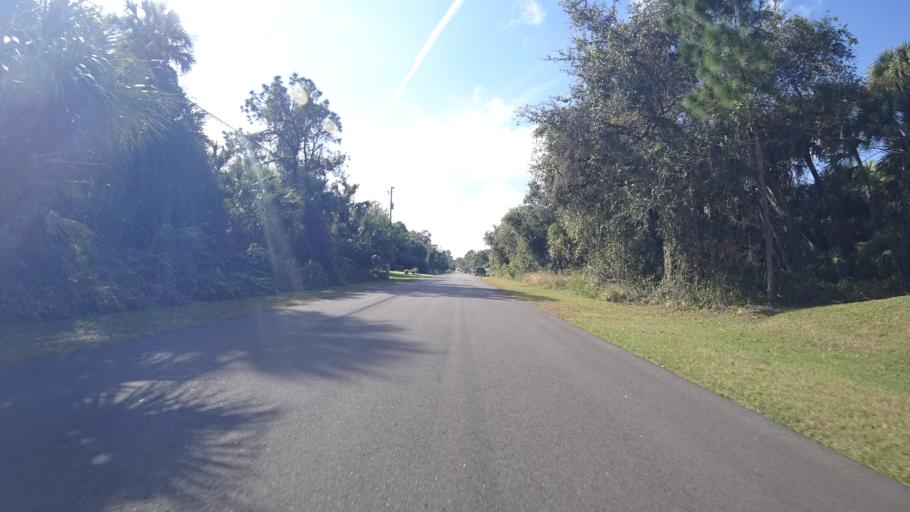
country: US
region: Florida
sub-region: Charlotte County
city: Port Charlotte
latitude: 27.0662
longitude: -82.1145
